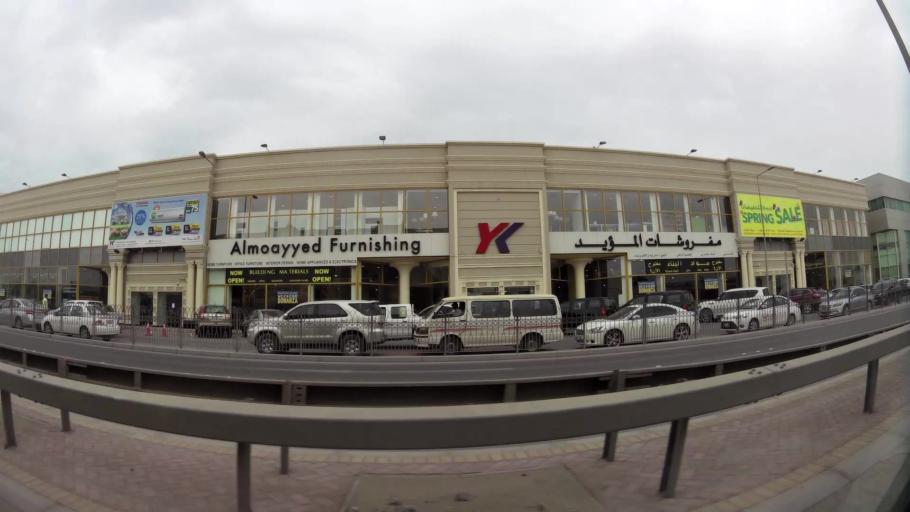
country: BH
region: Manama
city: Jidd Hafs
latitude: 26.2072
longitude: 50.5417
